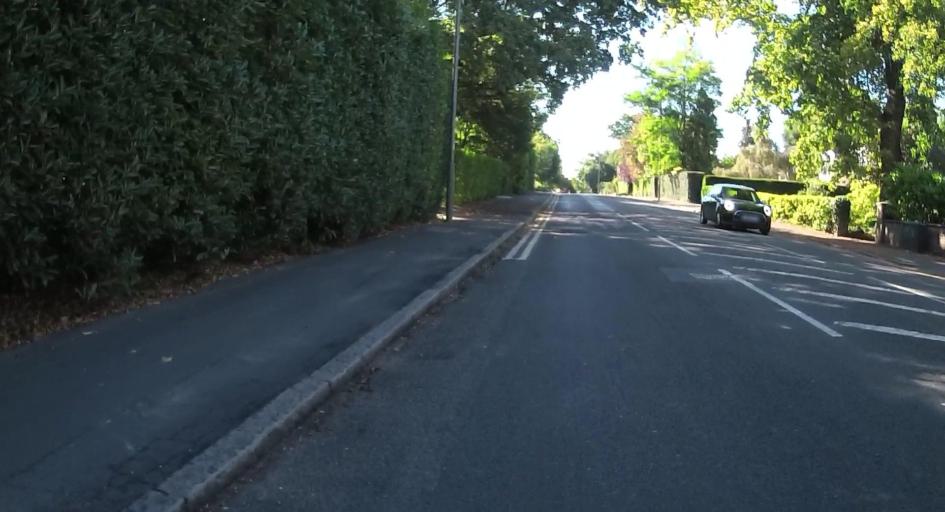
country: GB
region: England
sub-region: Surrey
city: Walton-on-Thames
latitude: 51.3746
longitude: -0.4213
